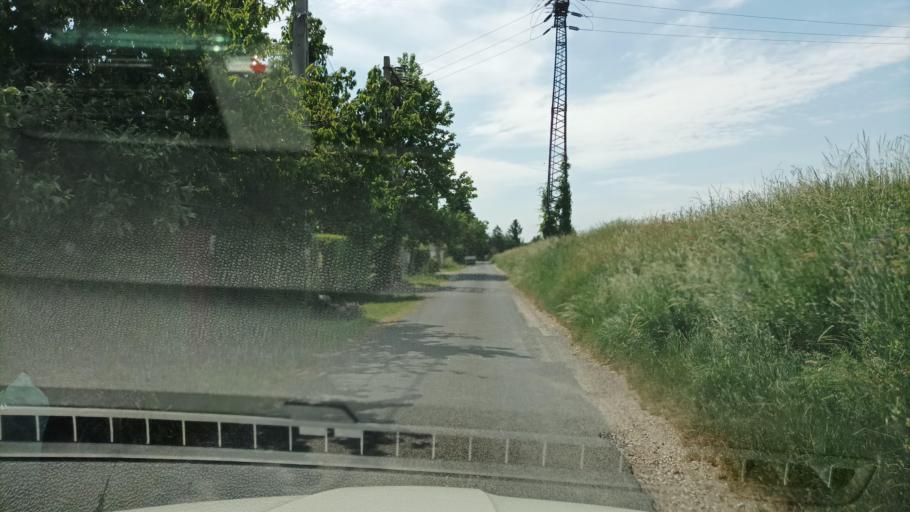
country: HU
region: Pest
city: Rackeve
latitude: 47.1344
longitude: 18.9619
